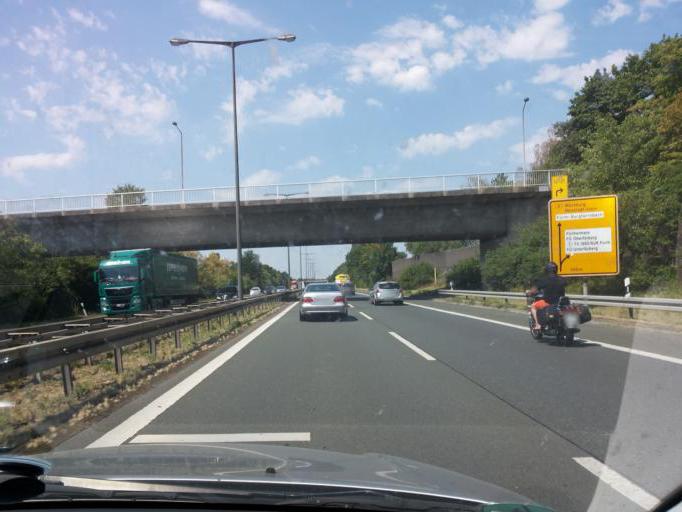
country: DE
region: Bavaria
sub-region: Regierungsbezirk Mittelfranken
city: Zirndorf
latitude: 49.4630
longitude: 10.9637
